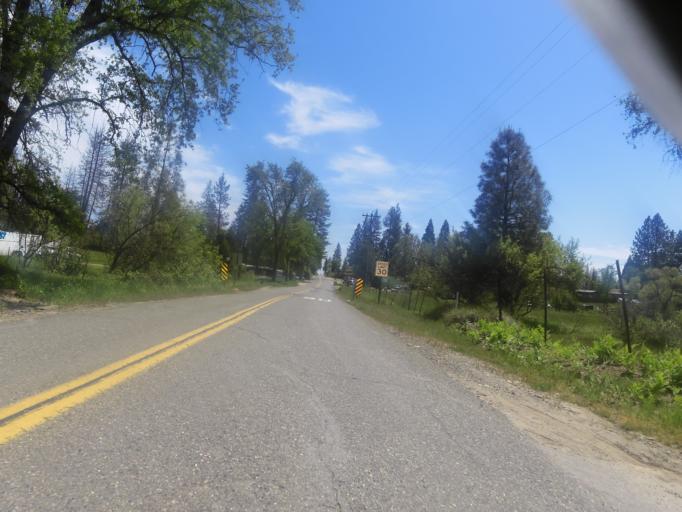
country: US
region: California
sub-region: Mariposa County
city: Midpines
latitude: 37.4907
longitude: -119.8121
